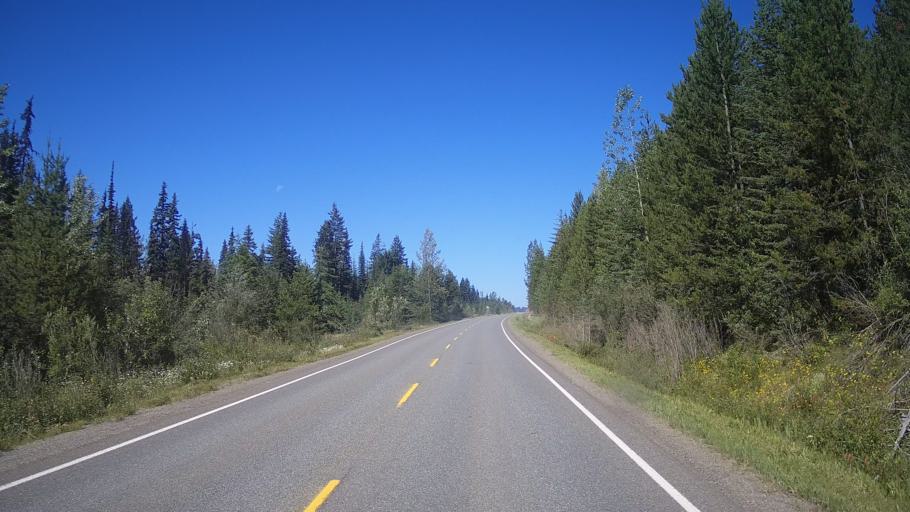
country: CA
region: British Columbia
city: Kamloops
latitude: 51.4965
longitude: -120.3893
